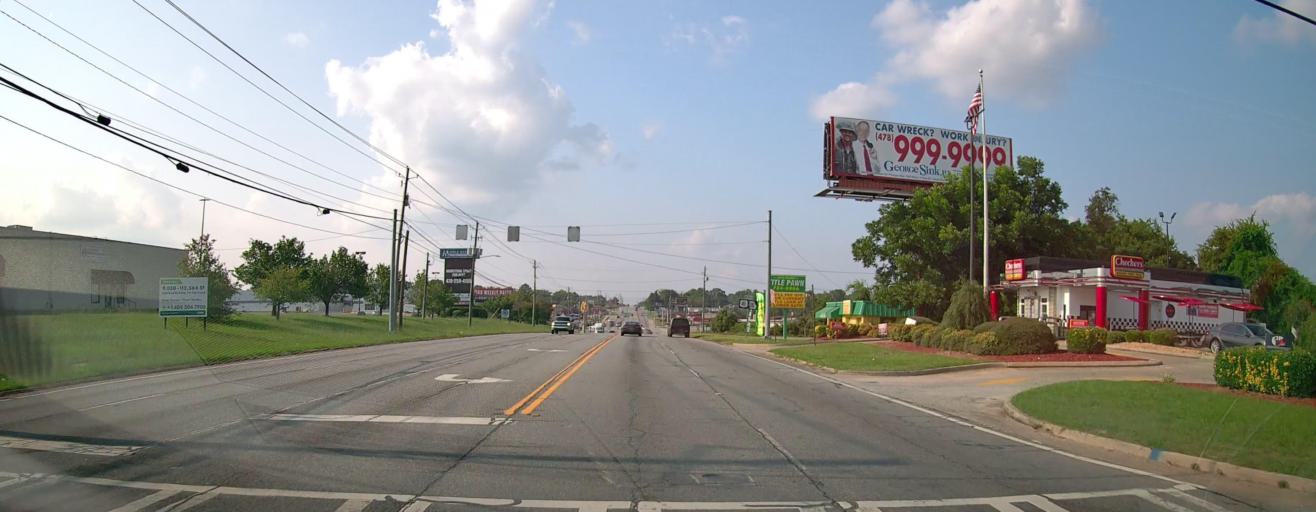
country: US
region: Georgia
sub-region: Bibb County
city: Macon
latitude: 32.8114
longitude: -83.6629
